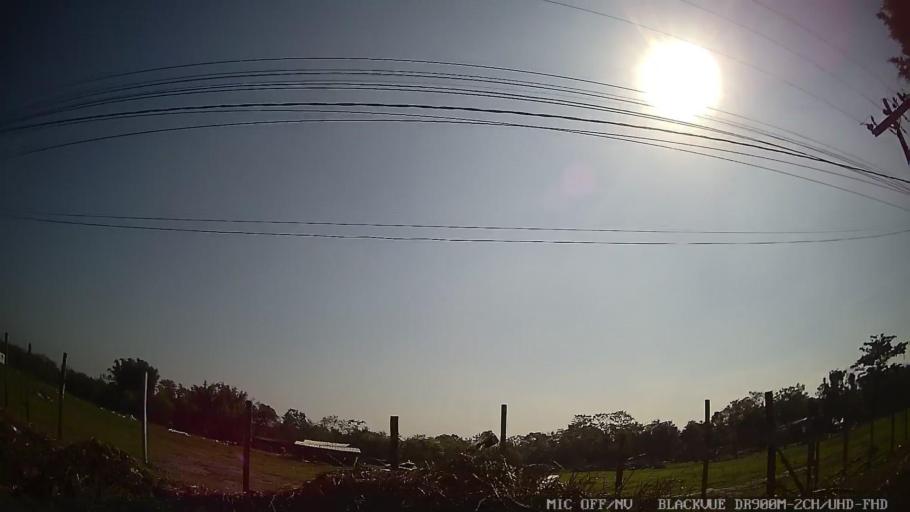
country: BR
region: Sao Paulo
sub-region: Guaruja
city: Guaruja
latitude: -24.0081
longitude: -46.2878
